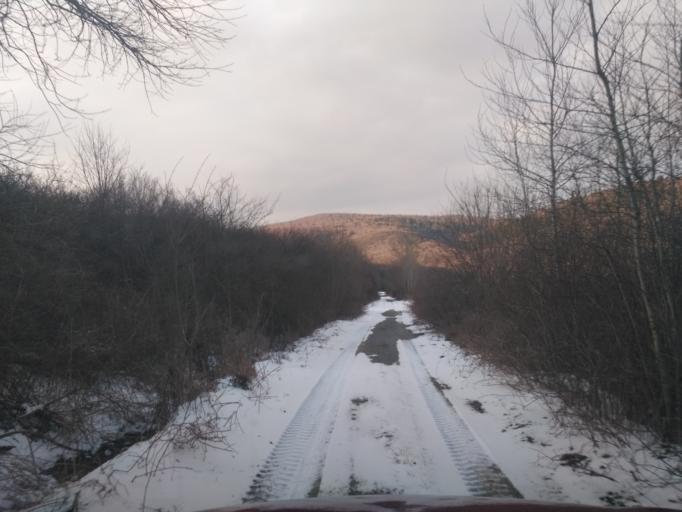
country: SK
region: Kosicky
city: Kosice
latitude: 48.7409
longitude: 21.1503
